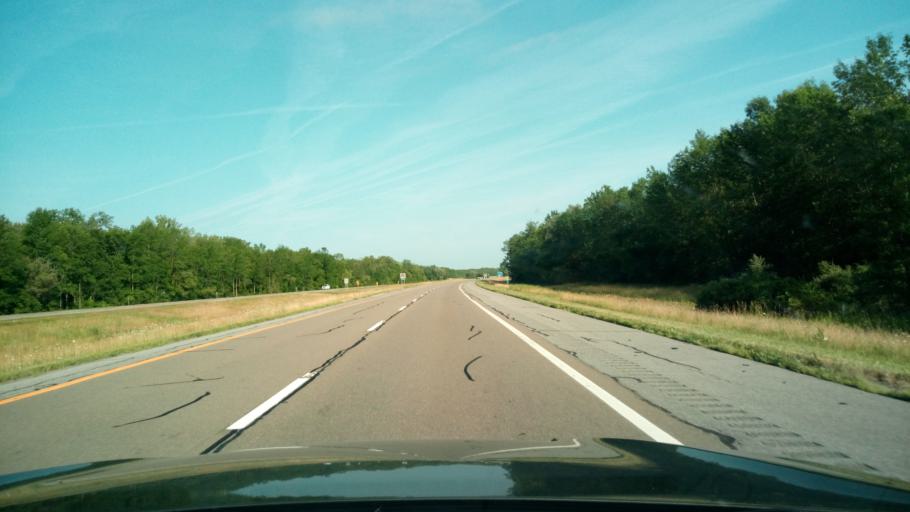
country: US
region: New York
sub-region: Livingston County
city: Mount Morris
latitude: 42.6980
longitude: -77.8183
